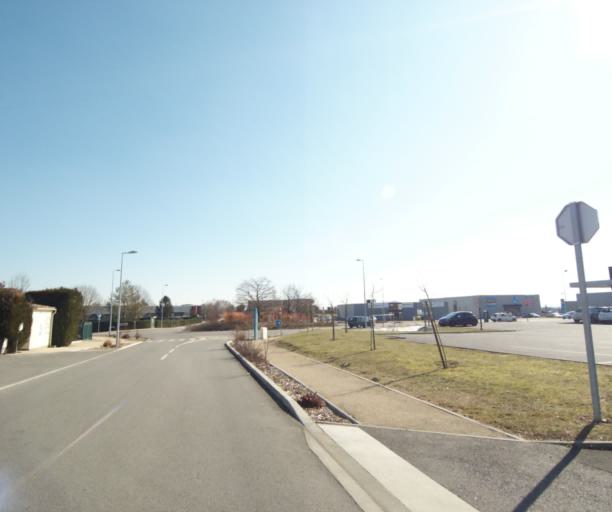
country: FR
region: Poitou-Charentes
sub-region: Departement des Deux-Sevres
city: Chauray
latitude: 46.3383
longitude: -0.3984
